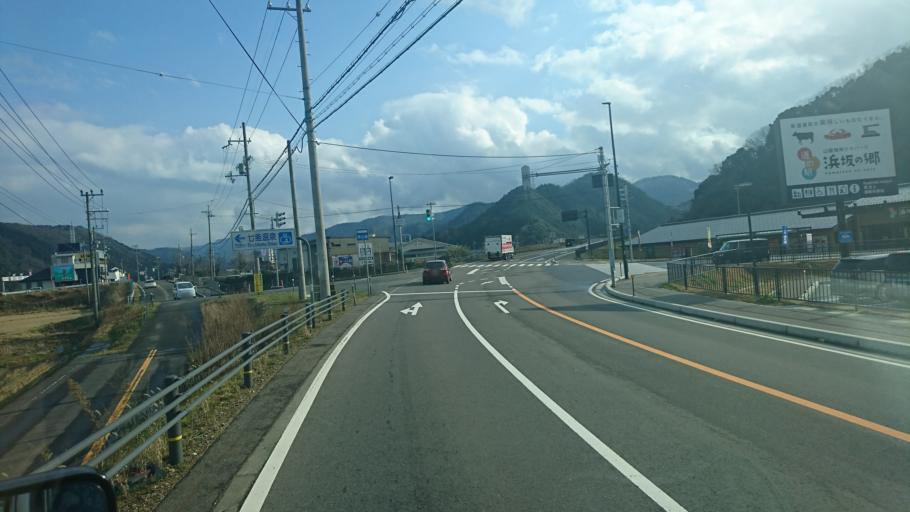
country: JP
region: Tottori
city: Tottori
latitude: 35.6106
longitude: 134.4702
